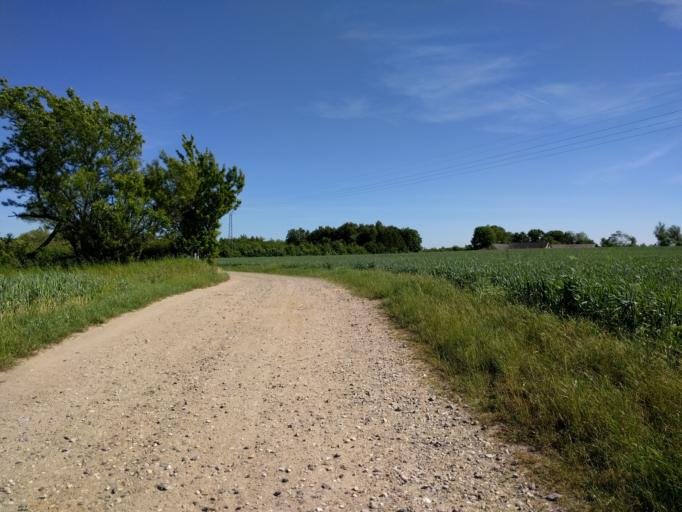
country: DK
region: South Denmark
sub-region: Kerteminde Kommune
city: Langeskov
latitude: 55.3777
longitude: 10.5976
